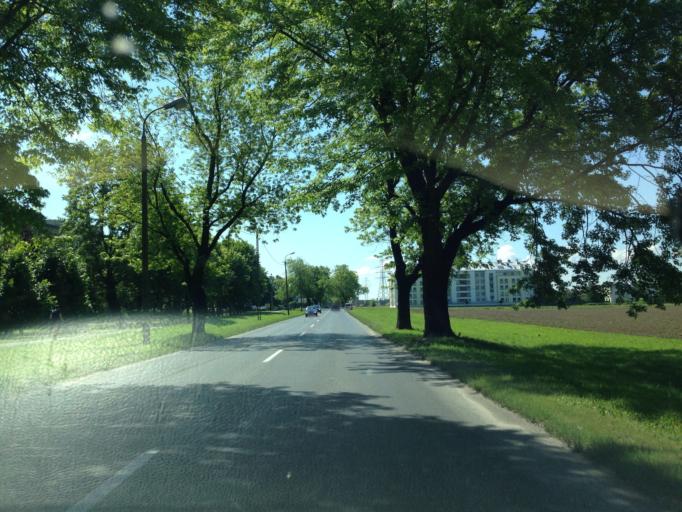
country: PL
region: Masovian Voivodeship
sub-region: Warszawa
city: Bemowo
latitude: 52.2353
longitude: 20.8967
